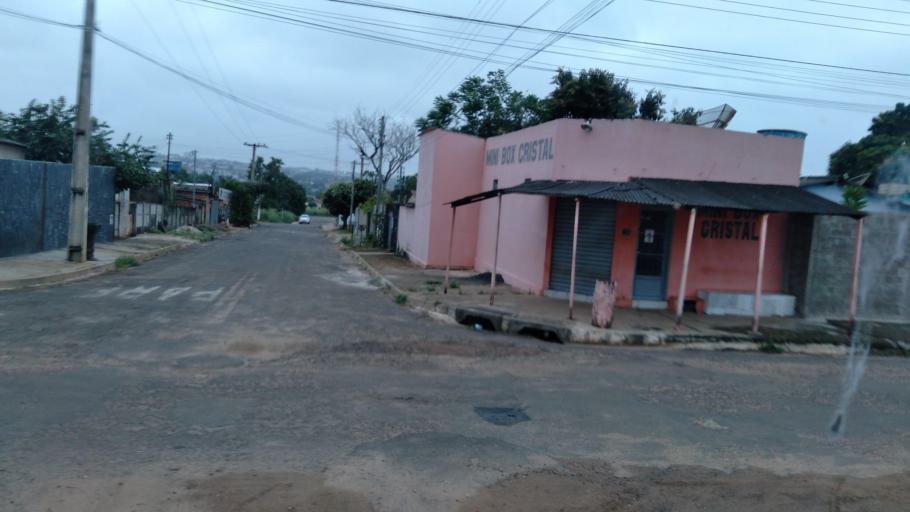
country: BR
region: Goias
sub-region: Mineiros
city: Mineiros
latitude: -17.5781
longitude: -52.5450
